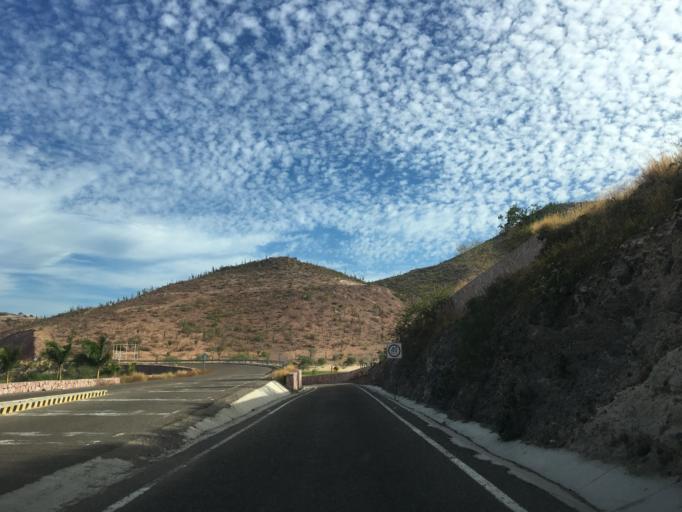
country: MX
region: Baja California Sur
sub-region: La Paz
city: La Paz
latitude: 24.2125
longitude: -110.2955
